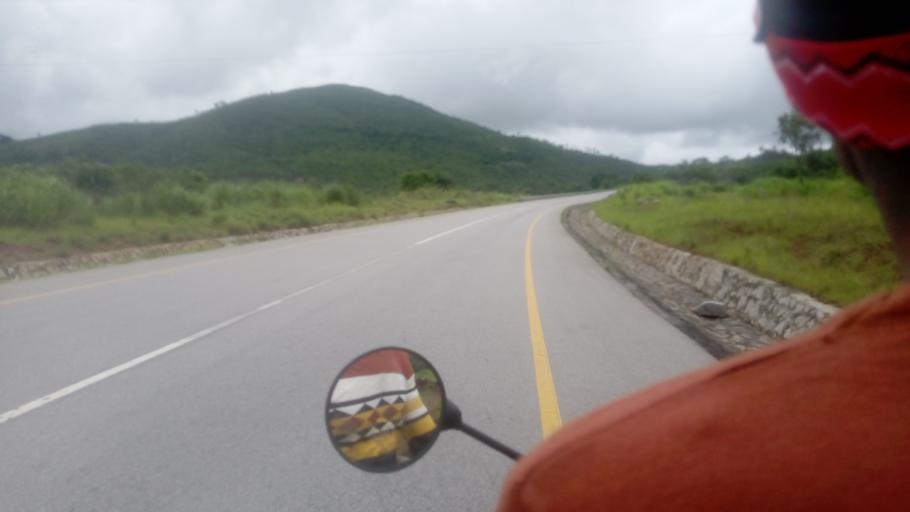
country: SL
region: Northern Province
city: Masaka
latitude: 8.6621
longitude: -11.7996
